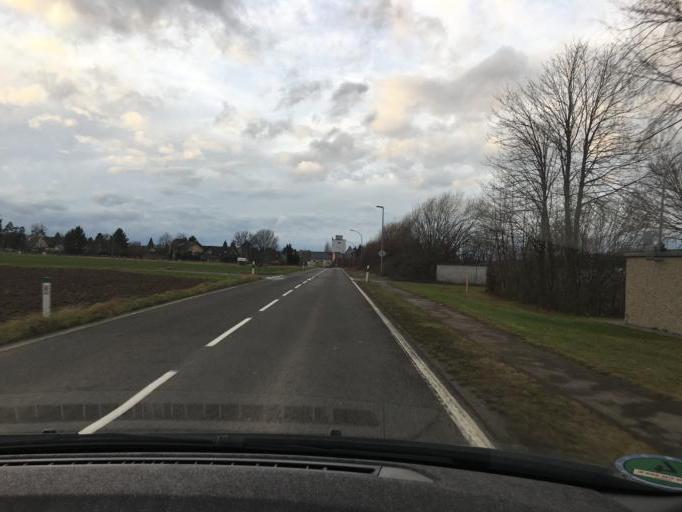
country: DE
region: North Rhine-Westphalia
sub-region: Regierungsbezirk Koln
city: Bad Munstereifel
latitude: 50.6031
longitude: 6.7466
